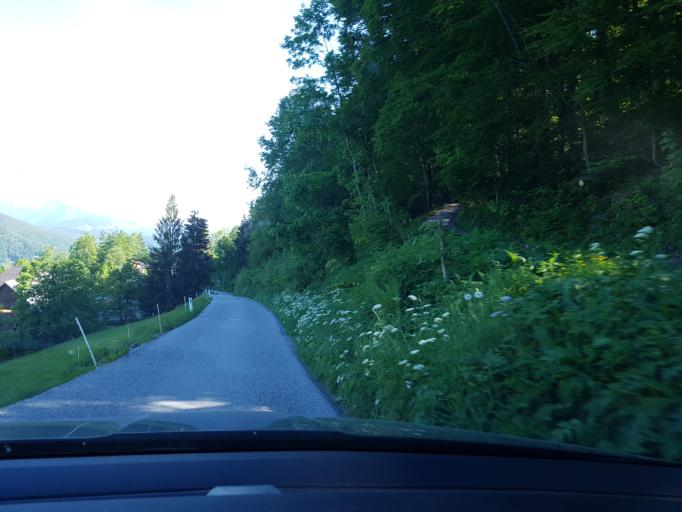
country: AT
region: Salzburg
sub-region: Politischer Bezirk Salzburg-Umgebung
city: Koppl
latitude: 47.7887
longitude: 13.1160
